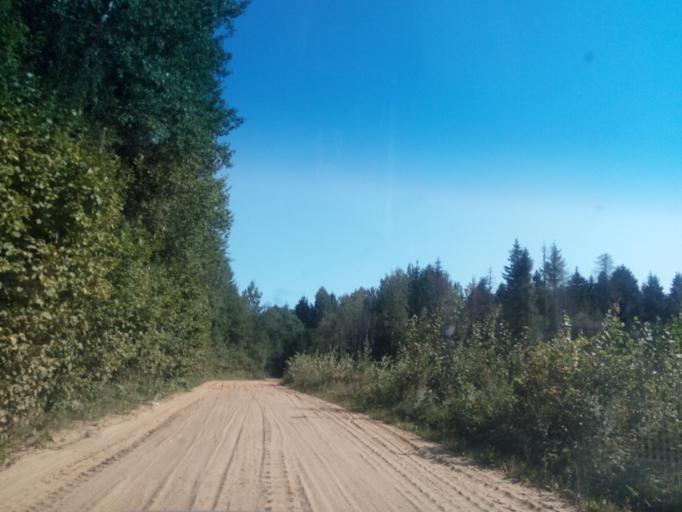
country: BY
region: Vitebsk
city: Dzisna
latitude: 55.6492
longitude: 28.3162
